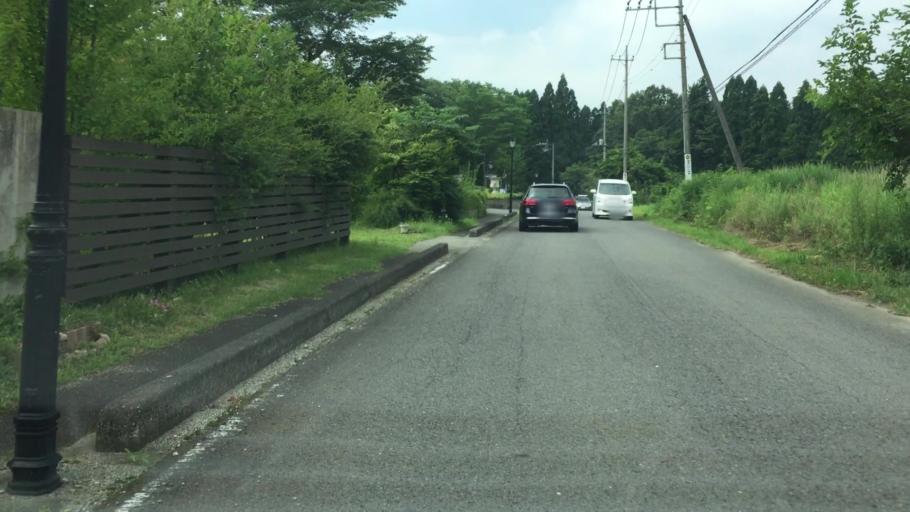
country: JP
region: Tochigi
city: Kuroiso
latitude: 37.0449
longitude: 140.0283
